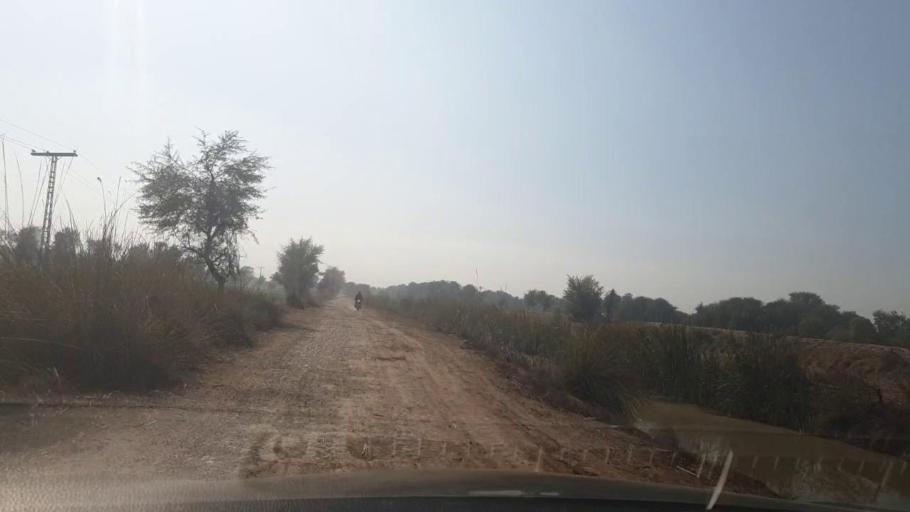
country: PK
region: Sindh
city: Ubauro
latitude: 28.1429
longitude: 69.6870
